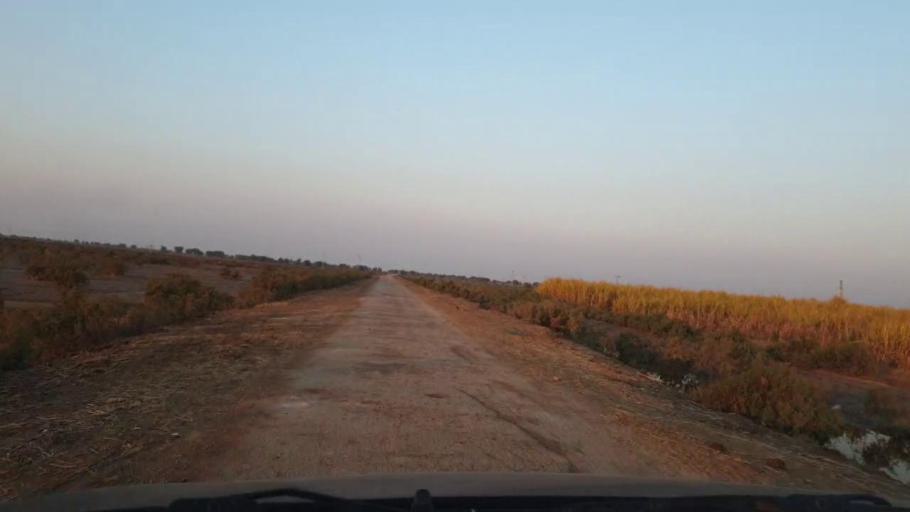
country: PK
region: Sindh
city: Jhol
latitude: 25.9273
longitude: 68.9660
